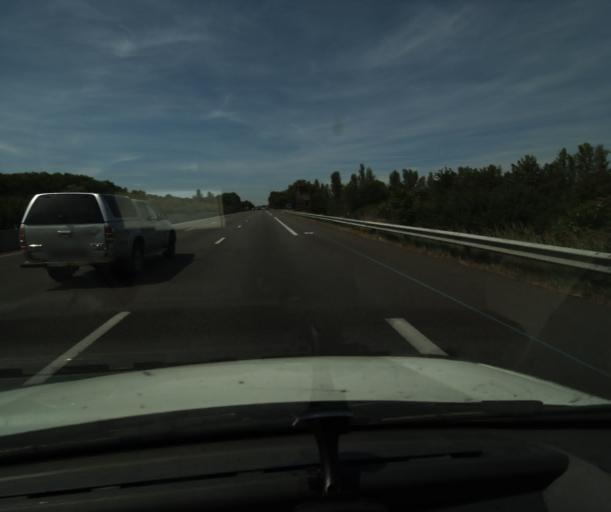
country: FR
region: Midi-Pyrenees
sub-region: Departement de la Haute-Garonne
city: Labege
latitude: 43.5202
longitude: 1.5227
